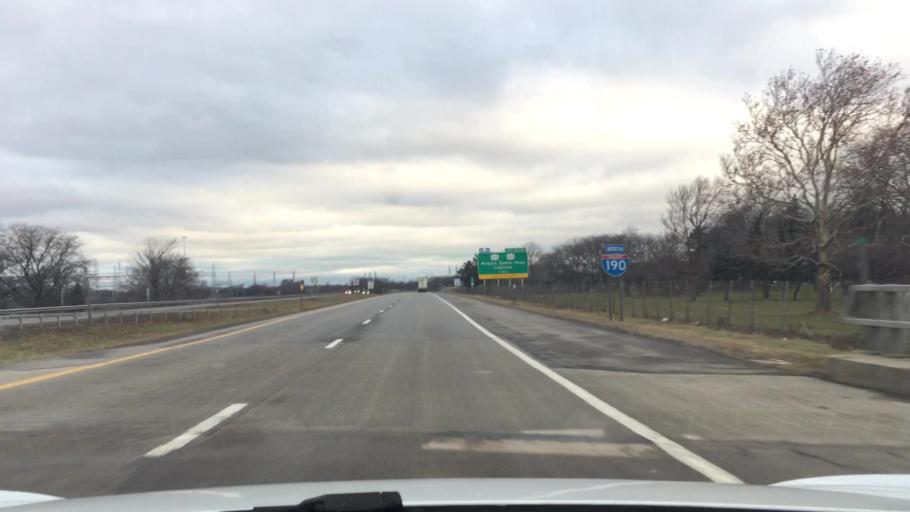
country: US
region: New York
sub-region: Niagara County
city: Lewiston
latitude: 43.1354
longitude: -79.0205
